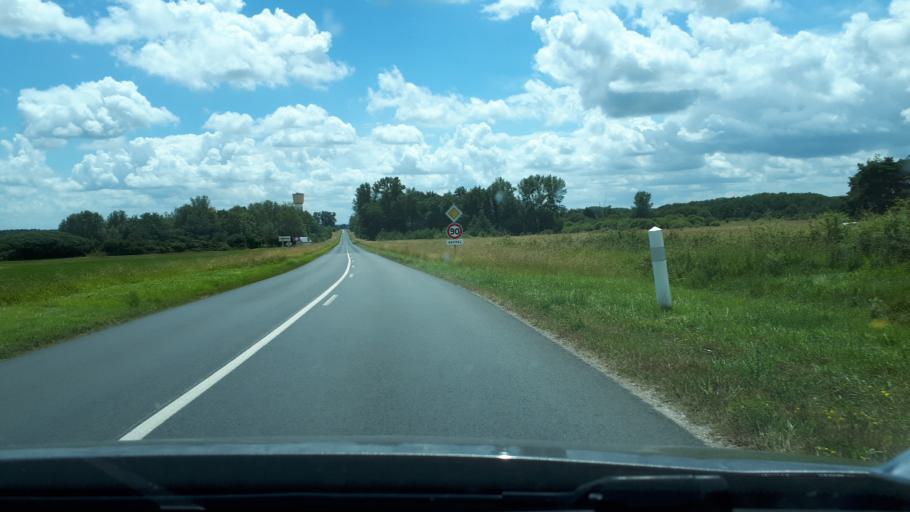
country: FR
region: Centre
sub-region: Departement du Loir-et-Cher
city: Contres
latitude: 47.3951
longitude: 1.4094
